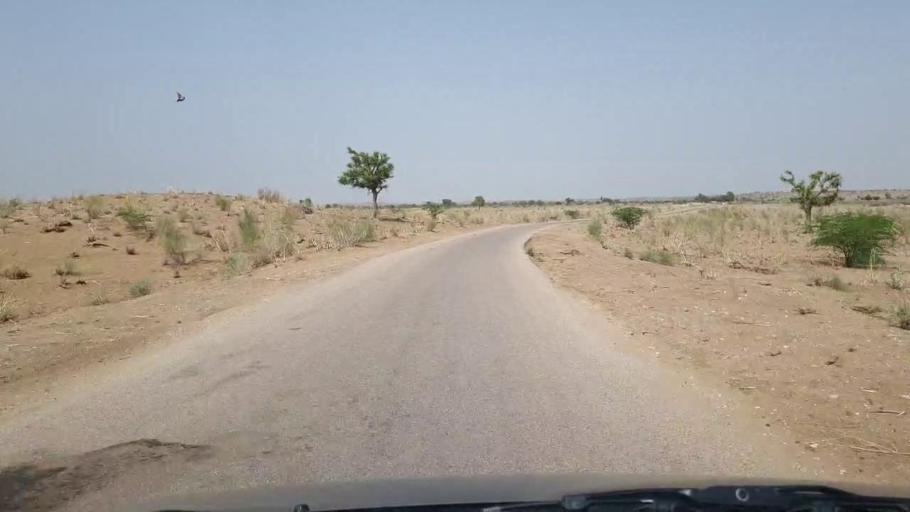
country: PK
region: Sindh
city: Chor
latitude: 25.4738
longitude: 70.5057
